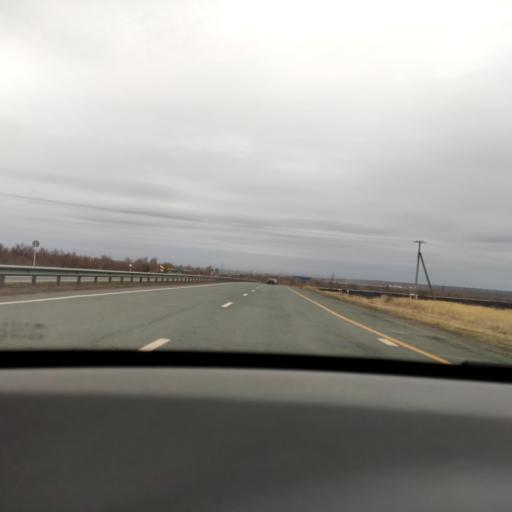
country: RU
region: Samara
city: Novokuybyshevsk
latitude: 53.0134
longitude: 49.9792
